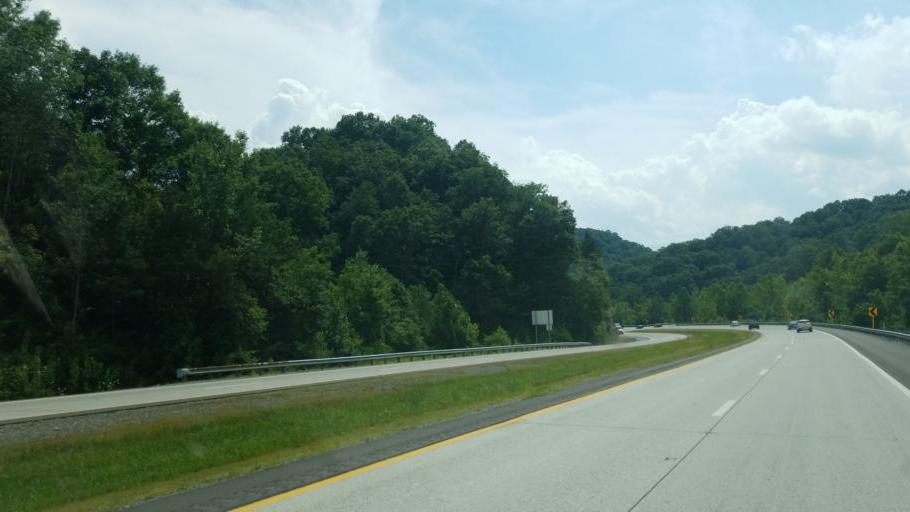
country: US
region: West Virginia
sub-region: Kanawha County
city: Alum Creek
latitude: 38.1994
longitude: -81.8417
